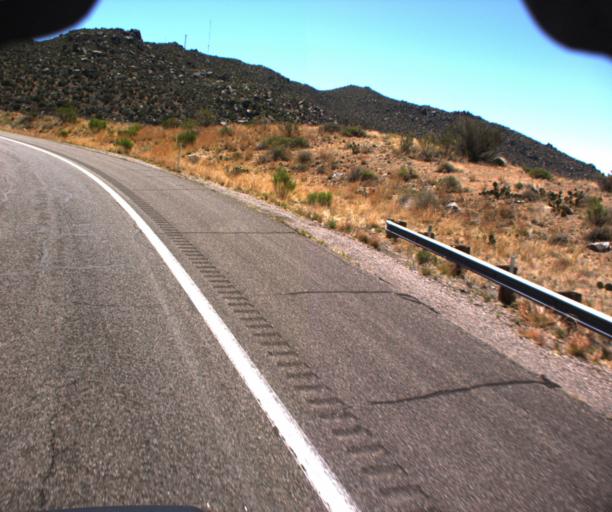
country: US
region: Arizona
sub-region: Yavapai County
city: Congress
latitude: 34.2006
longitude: -112.7649
